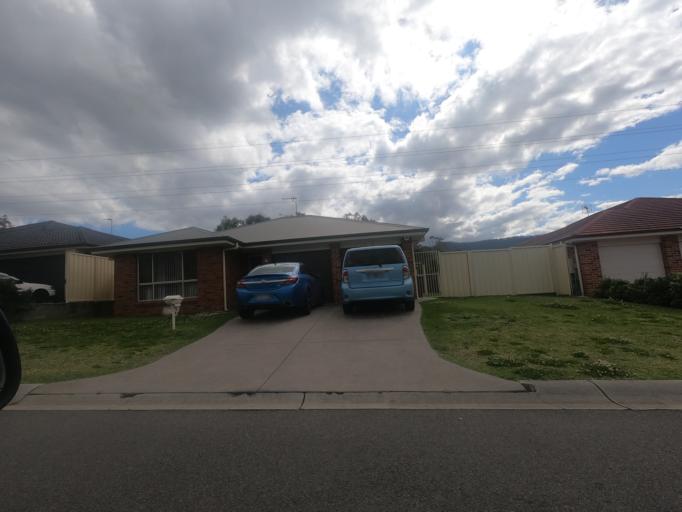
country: AU
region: New South Wales
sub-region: Wollongong
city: Dapto
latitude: -34.4880
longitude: 150.7724
